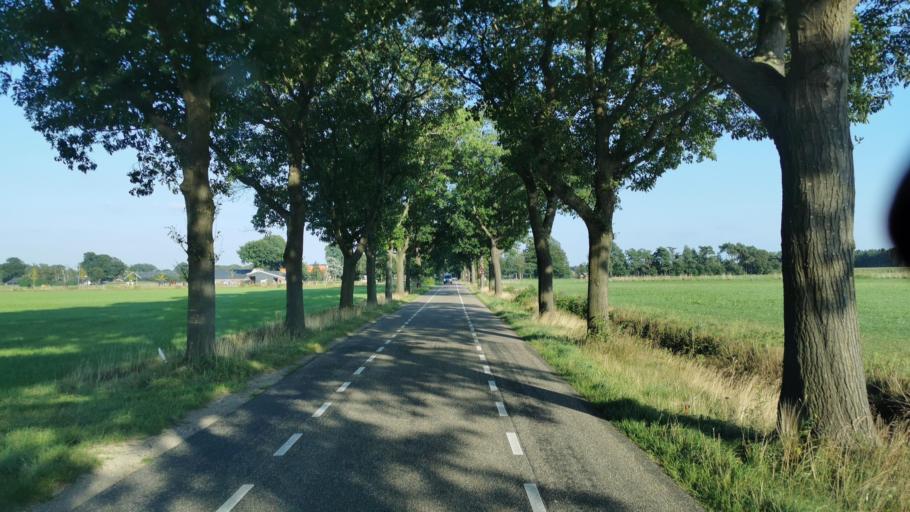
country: NL
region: Overijssel
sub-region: Gemeente Oldenzaal
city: Oldenzaal
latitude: 52.3197
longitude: 6.8749
